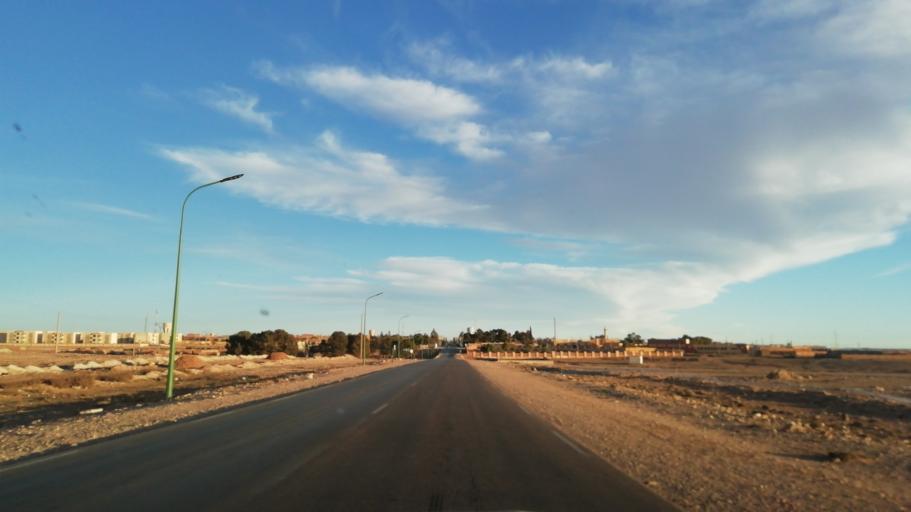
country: DZ
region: Wilaya de Naama
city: Naama
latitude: 33.7221
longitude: -0.7365
